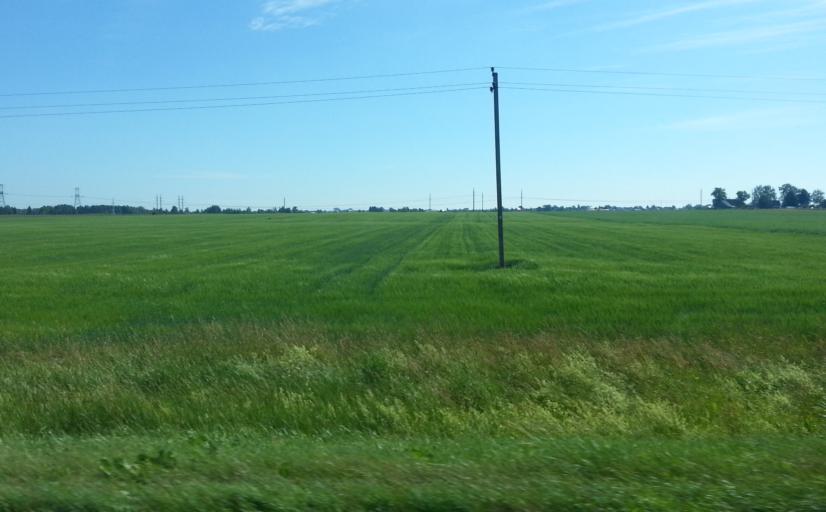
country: LT
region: Panevezys
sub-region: Panevezys City
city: Panevezys
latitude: 55.7082
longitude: 24.2707
